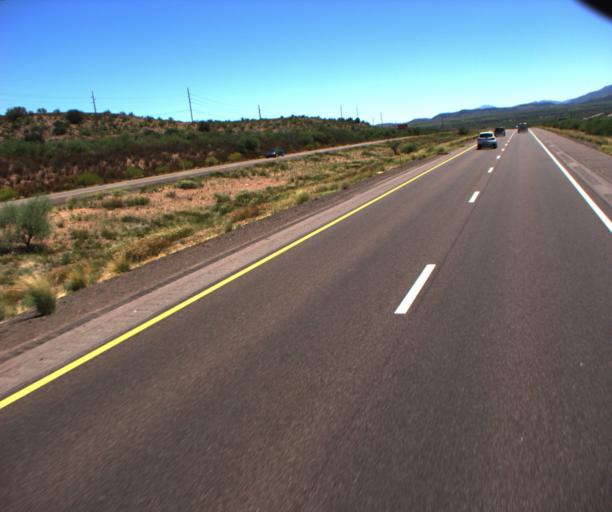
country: US
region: Arizona
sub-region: Gila County
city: Payson
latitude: 34.0984
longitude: -111.3538
